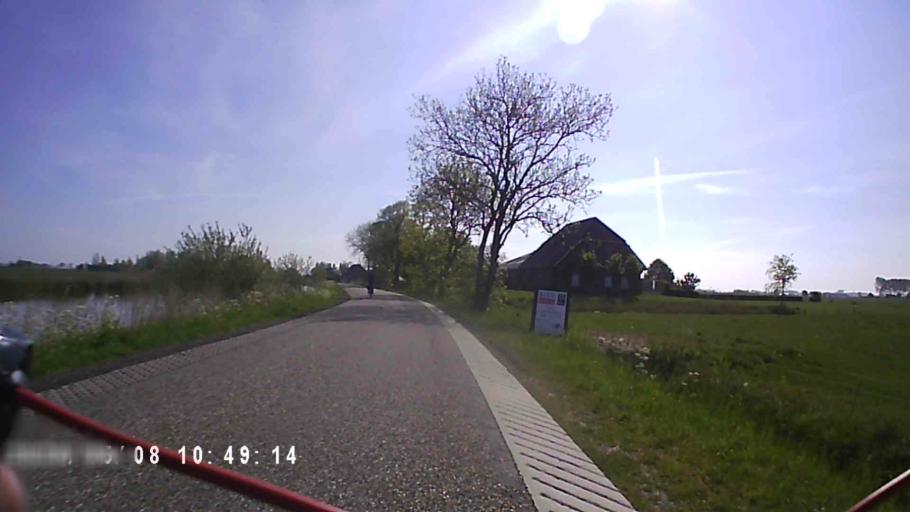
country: NL
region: Groningen
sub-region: Gemeente Winsum
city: Winsum
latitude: 53.3344
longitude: 6.5591
